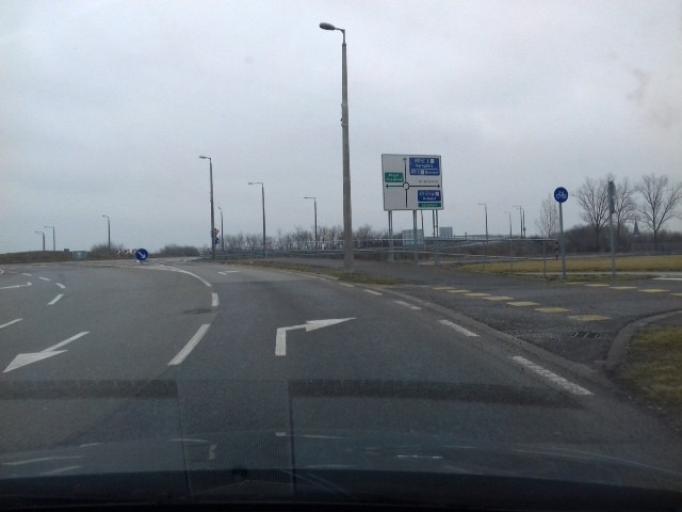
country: HU
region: Hajdu-Bihar
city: Polgar
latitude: 47.8449
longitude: 21.1424
